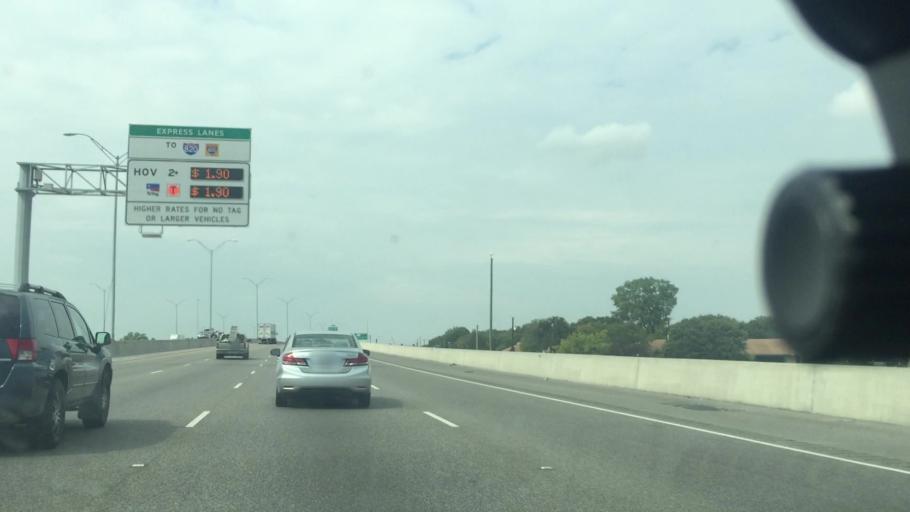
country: US
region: Texas
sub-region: Tarrant County
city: Hurst
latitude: 32.8401
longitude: -97.1646
